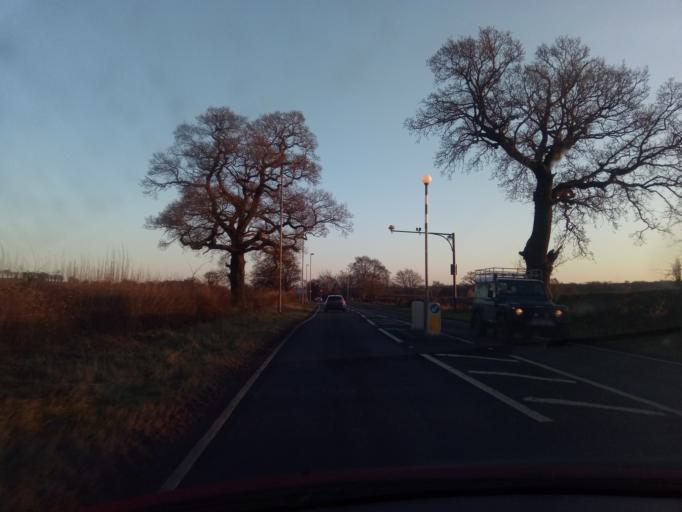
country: GB
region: England
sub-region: Nottinghamshire
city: Burton Joyce
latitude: 53.0365
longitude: -1.0499
